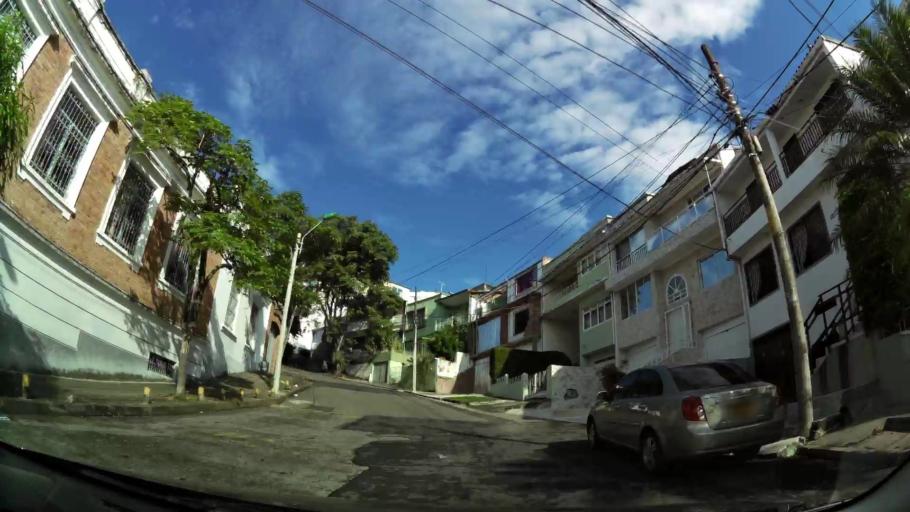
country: CO
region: Valle del Cauca
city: Cali
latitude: 3.4381
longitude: -76.5419
